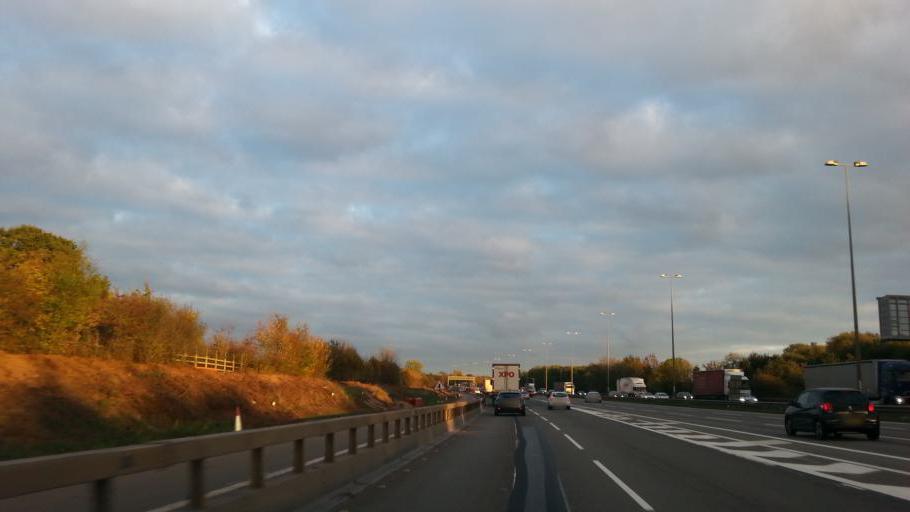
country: GB
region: England
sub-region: Solihull
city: Meriden
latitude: 52.4719
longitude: -1.6653
